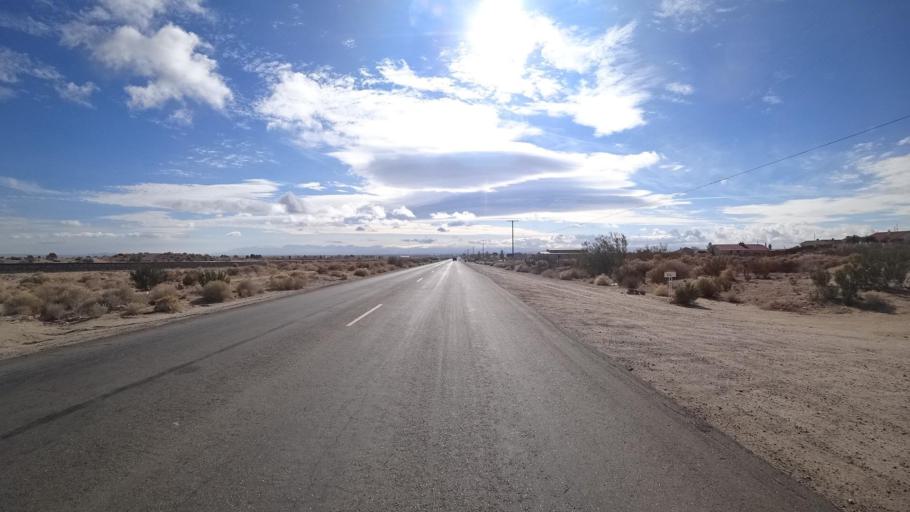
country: US
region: California
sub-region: Kern County
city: Rosamond
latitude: 34.8758
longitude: -118.1649
